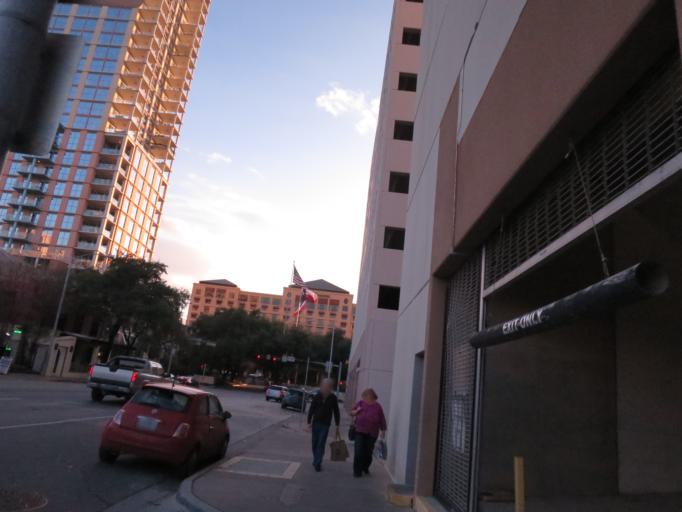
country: US
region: Texas
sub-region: Travis County
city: Austin
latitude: 30.2634
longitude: -97.7420
